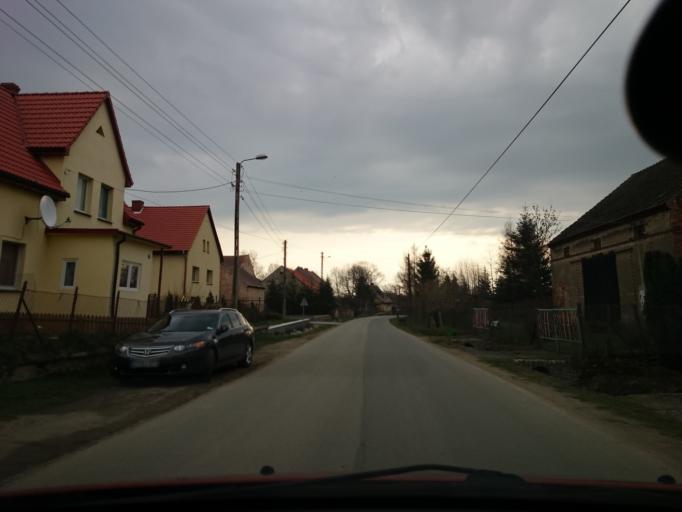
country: PL
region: Lower Silesian Voivodeship
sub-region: Powiat zabkowicki
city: Bardo
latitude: 50.5283
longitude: 16.7576
